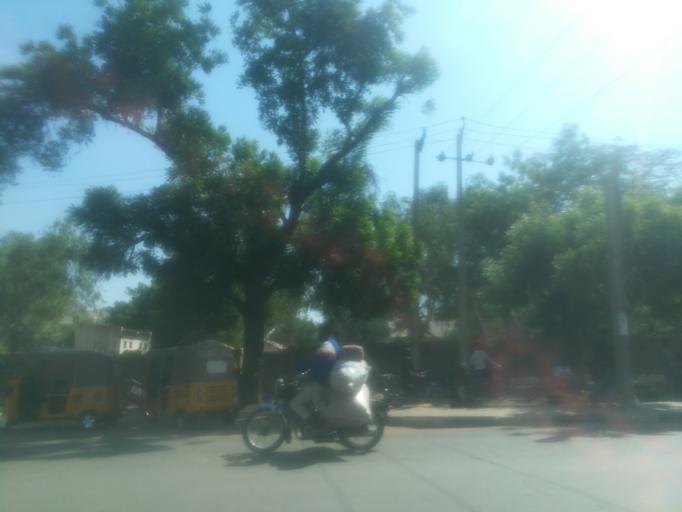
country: NG
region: Kano
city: Kano
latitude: 12.0117
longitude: 8.5430
